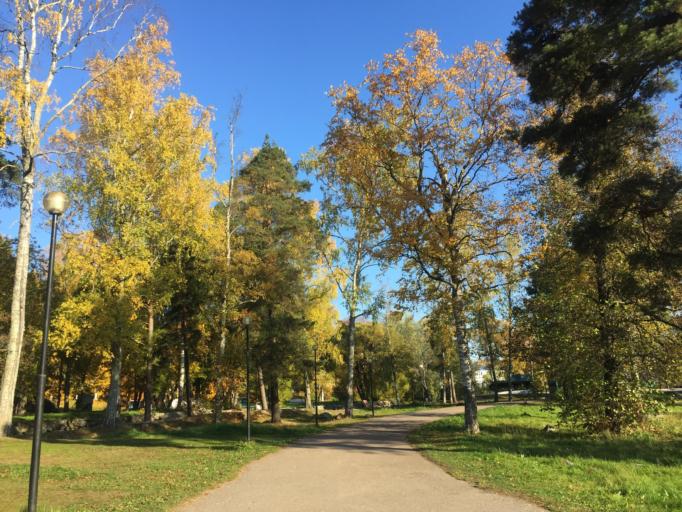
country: RU
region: Leningrad
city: Priozersk
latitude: 61.0308
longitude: 30.1223
